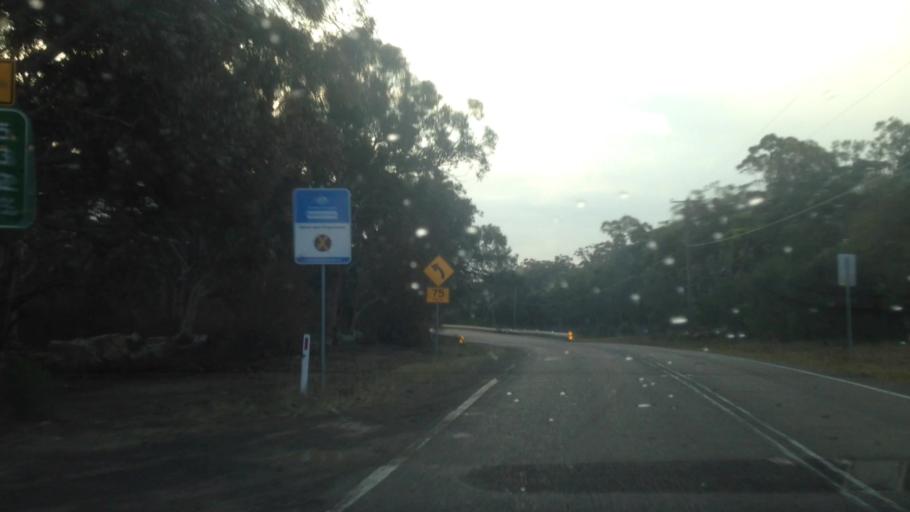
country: AU
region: New South Wales
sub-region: Wyong Shire
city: Buff Point
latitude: -33.1968
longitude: 151.5209
